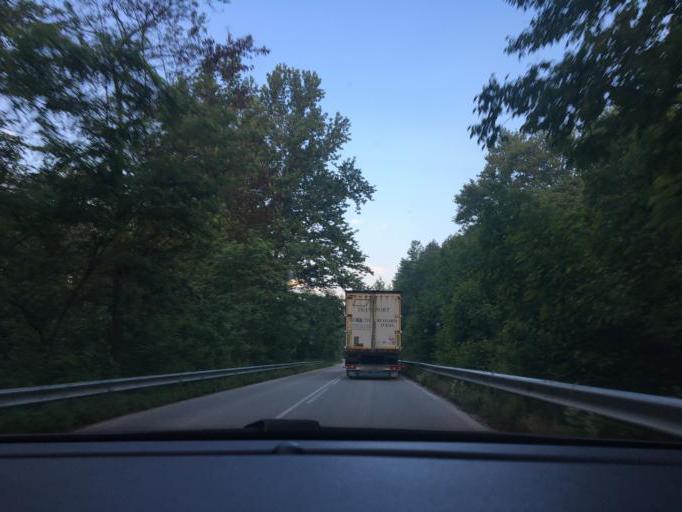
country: BG
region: Blagoevgrad
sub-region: Obshtina Petrich
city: Petrich
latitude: 41.3994
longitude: 23.0736
